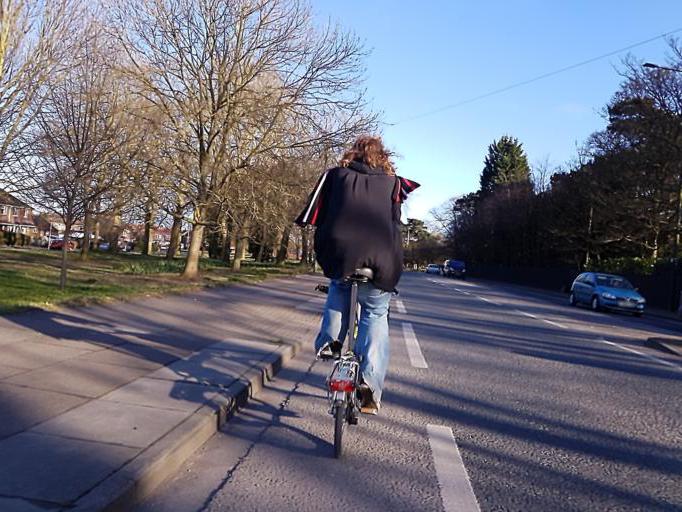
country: GB
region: England
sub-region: North East Lincolnshire
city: Grimsby
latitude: 53.5531
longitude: -0.0656
